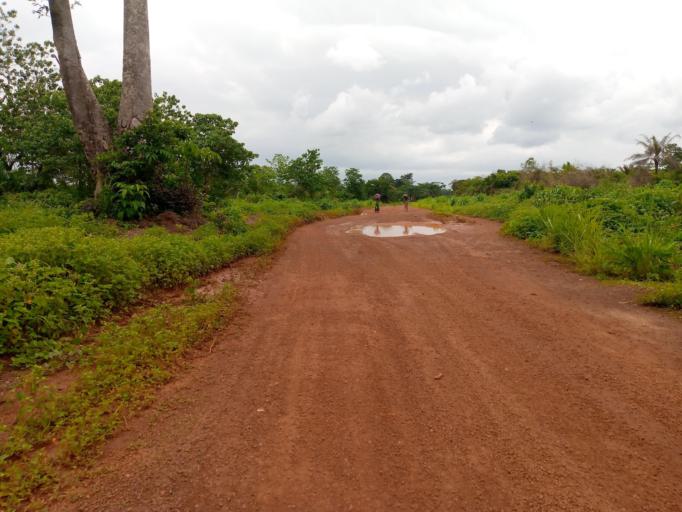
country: SL
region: Southern Province
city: Moyamba
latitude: 8.0831
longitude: -12.4510
